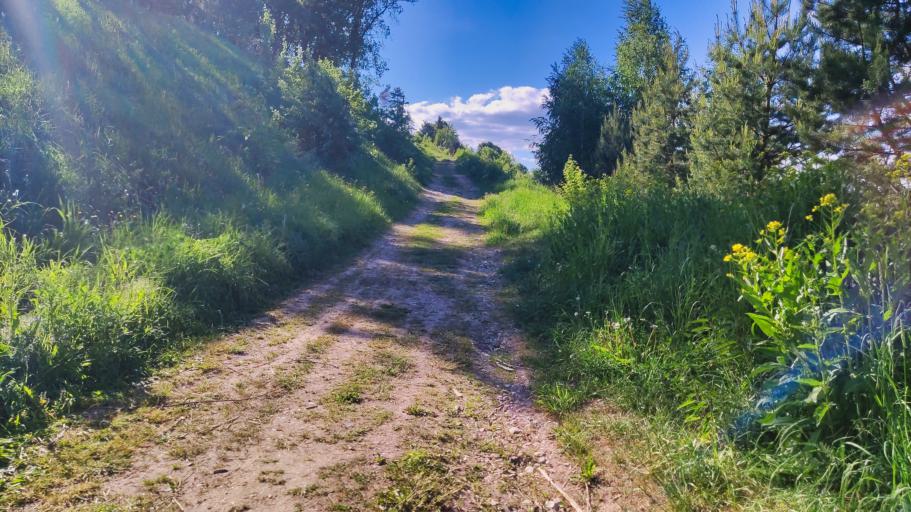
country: RU
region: Tverskaya
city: Rzhev
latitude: 56.2518
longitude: 34.3446
